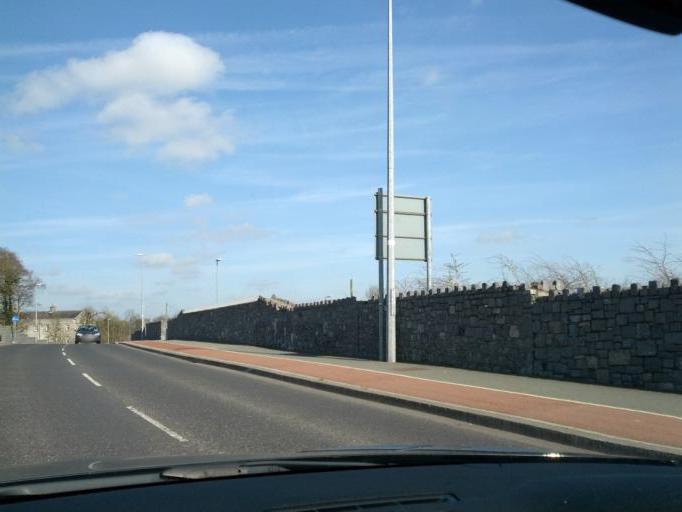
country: IE
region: Leinster
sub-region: Kildare
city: Maynooth
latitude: 53.3760
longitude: -6.5966
